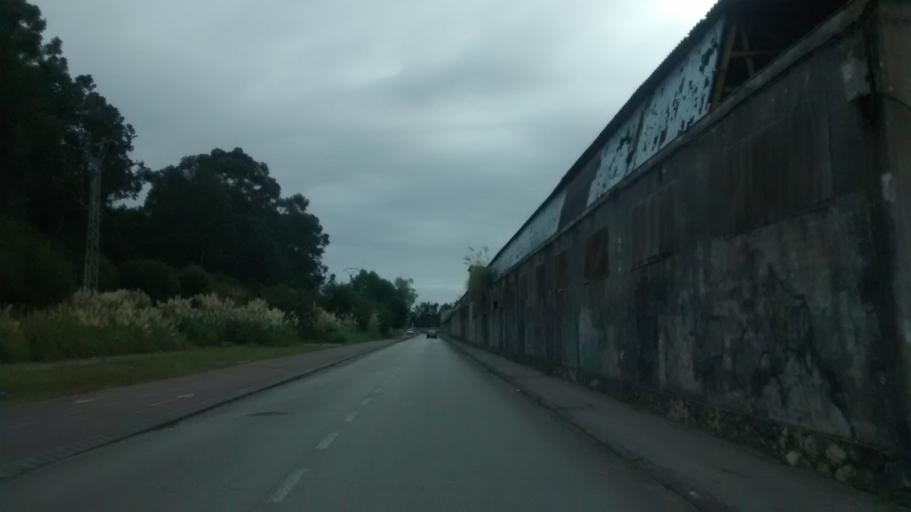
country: ES
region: Cantabria
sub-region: Provincia de Cantabria
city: El Astillero
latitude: 43.4184
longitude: -3.8138
